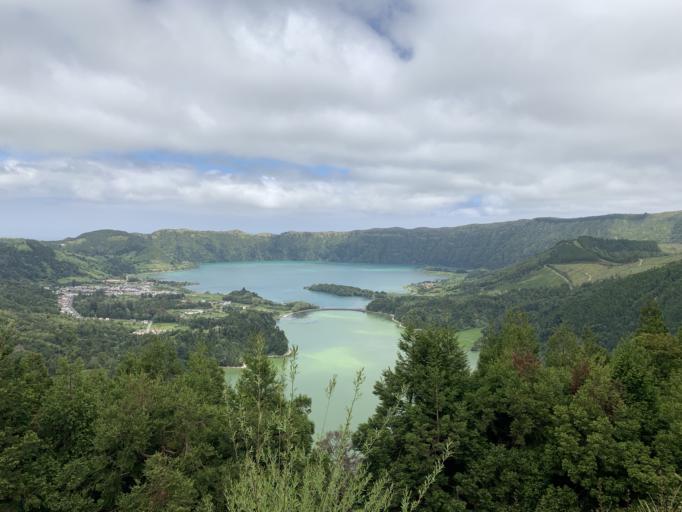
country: PT
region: Azores
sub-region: Ponta Delgada
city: Arrifes
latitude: 37.8394
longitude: -25.7949
